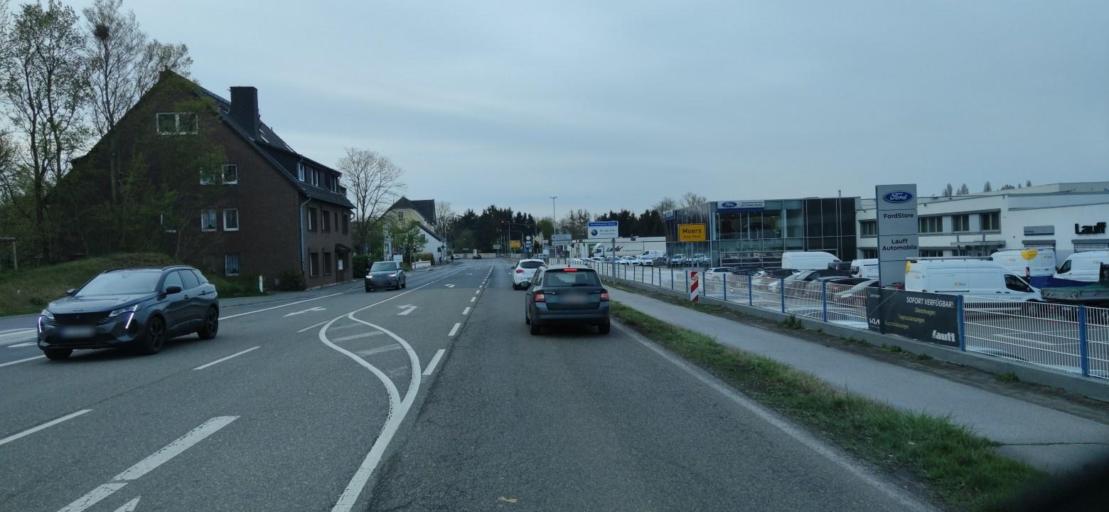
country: DE
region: North Rhine-Westphalia
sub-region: Regierungsbezirk Dusseldorf
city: Moers
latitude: 51.4593
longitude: 6.6223
